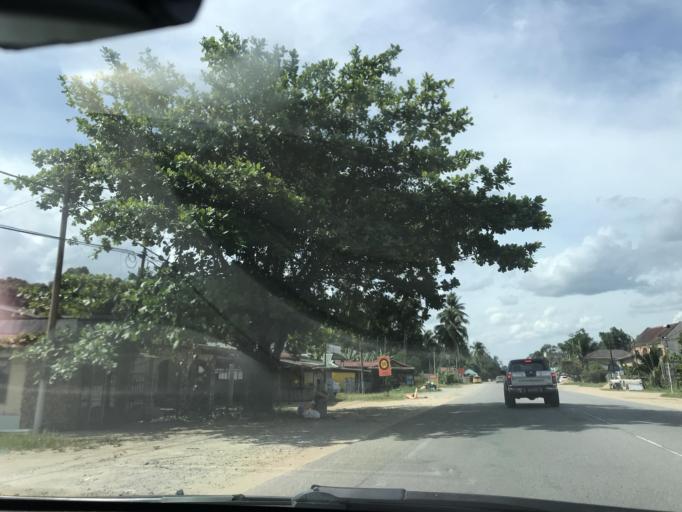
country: MY
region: Kelantan
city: Tanah Merah
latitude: 5.8490
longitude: 102.1635
